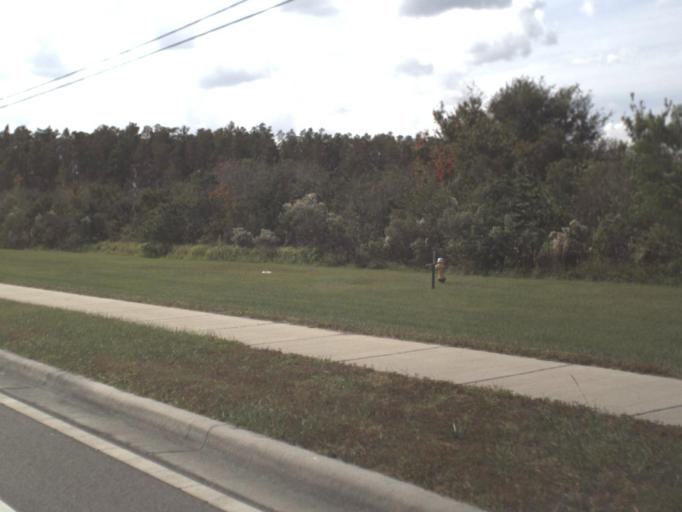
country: US
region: Florida
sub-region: Osceola County
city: Campbell
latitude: 28.2332
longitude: -81.4874
